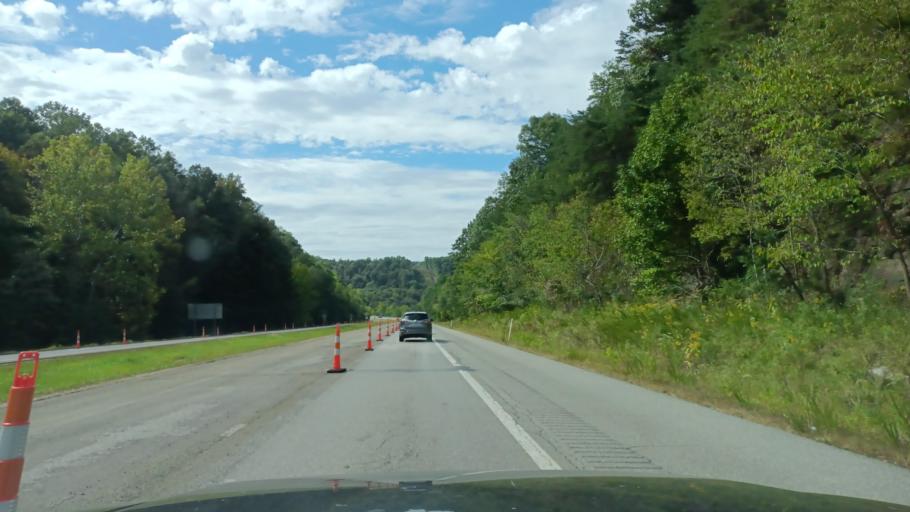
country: US
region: West Virginia
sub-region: Ritchie County
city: Harrisville
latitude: 39.2615
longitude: -81.0942
